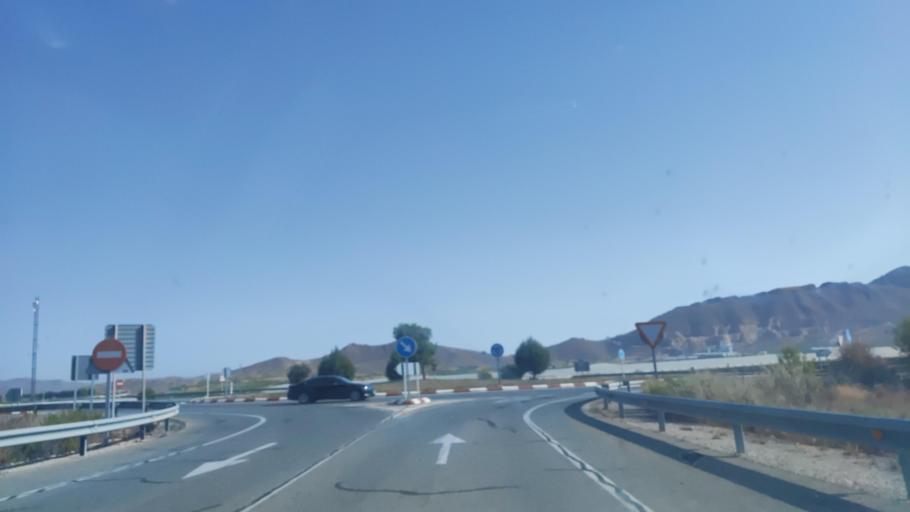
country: ES
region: Castille-La Mancha
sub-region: Provincia de Albacete
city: Hellin
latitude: 38.4635
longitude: -1.5933
